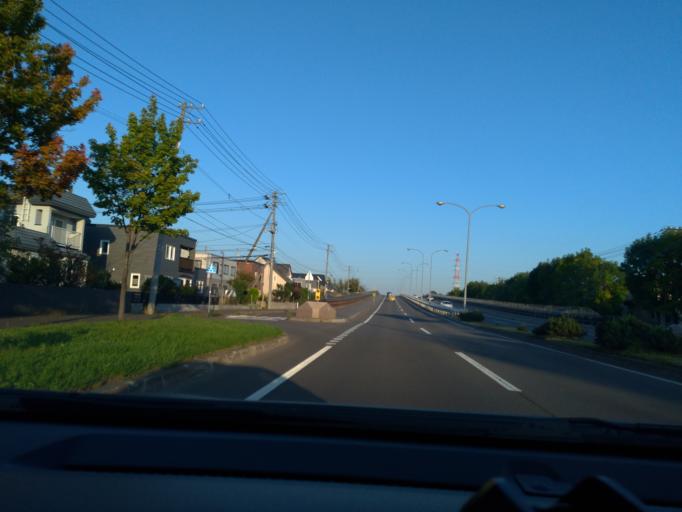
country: JP
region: Hokkaido
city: Ishikari
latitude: 43.1577
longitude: 141.4051
